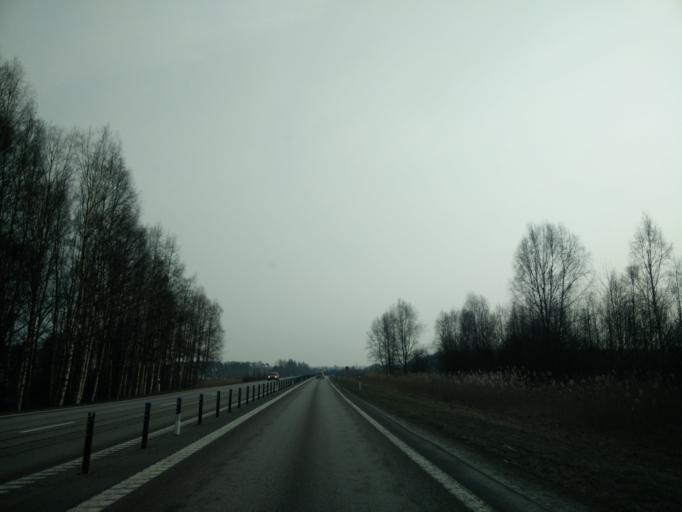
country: SE
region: Vaermland
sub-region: Karlstads Kommun
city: Karlstad
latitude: 59.4342
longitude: 13.4131
